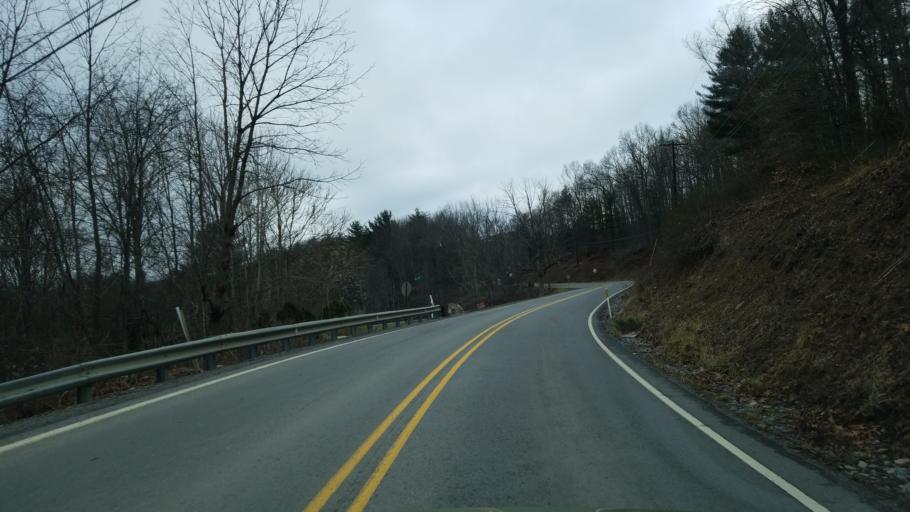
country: US
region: Pennsylvania
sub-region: Clearfield County
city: Clearfield
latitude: 41.0316
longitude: -78.4594
